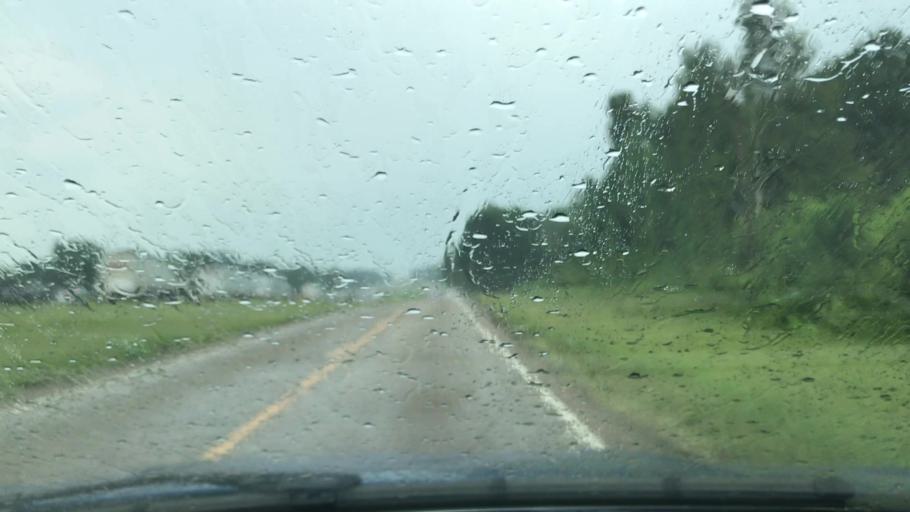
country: US
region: Texas
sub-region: Harrison County
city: Waskom
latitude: 32.4881
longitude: -94.1370
